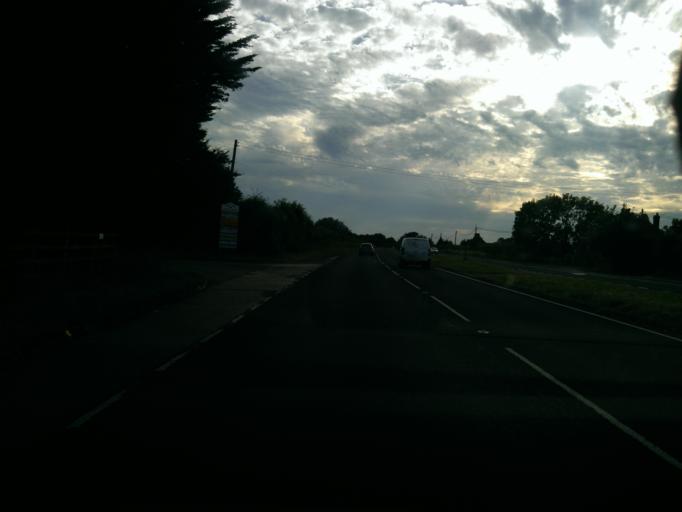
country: GB
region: England
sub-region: Essex
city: Wivenhoe
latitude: 51.8814
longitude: 0.9658
